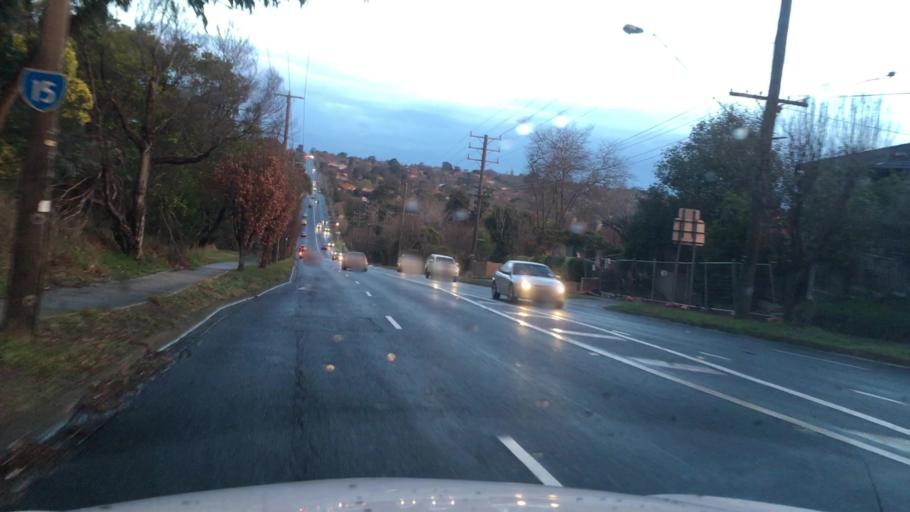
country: AU
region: Victoria
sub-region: Whitehorse
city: Surrey Hills
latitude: -37.8364
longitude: 145.0982
